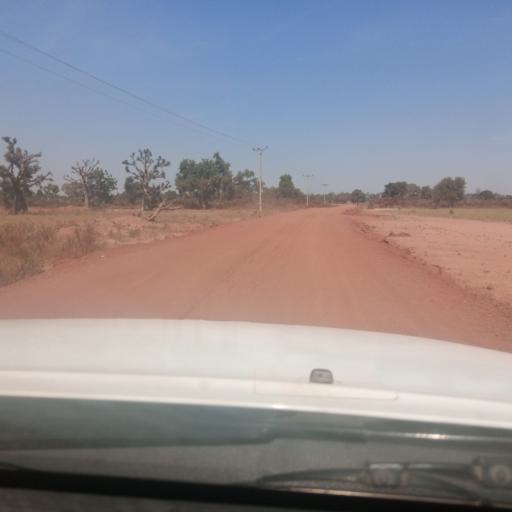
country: NG
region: Adamawa
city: Yola
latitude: 9.2036
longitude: 12.8775
